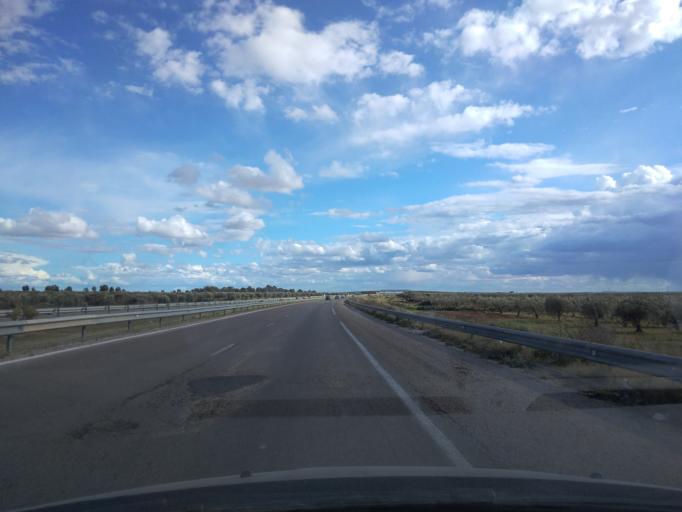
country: TN
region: Al Munastir
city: Manzil Kamil
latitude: 35.6266
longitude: 10.5916
